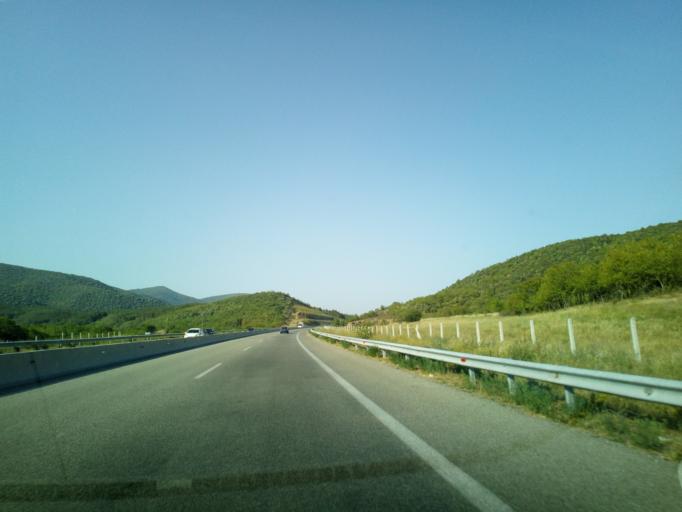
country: GR
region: Central Macedonia
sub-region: Nomos Thessalonikis
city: Nea Vrasna
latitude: 40.6886
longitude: 23.6241
